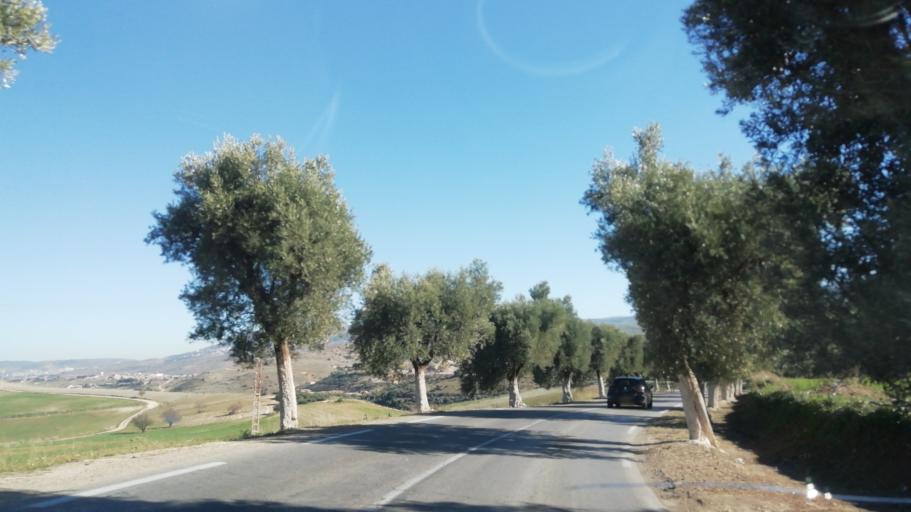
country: DZ
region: Tlemcen
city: Beni Mester
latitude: 34.8335
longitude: -1.5034
